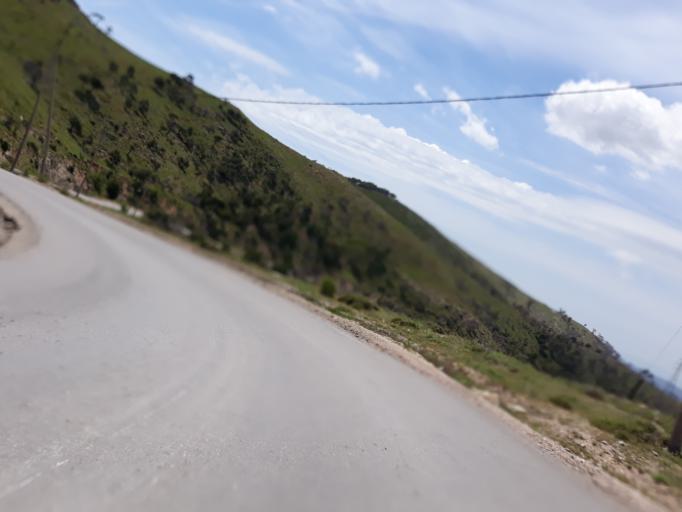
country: GR
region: Attica
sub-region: Nomarchia Dytikis Attikis
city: Magoula
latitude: 38.1633
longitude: 23.5391
